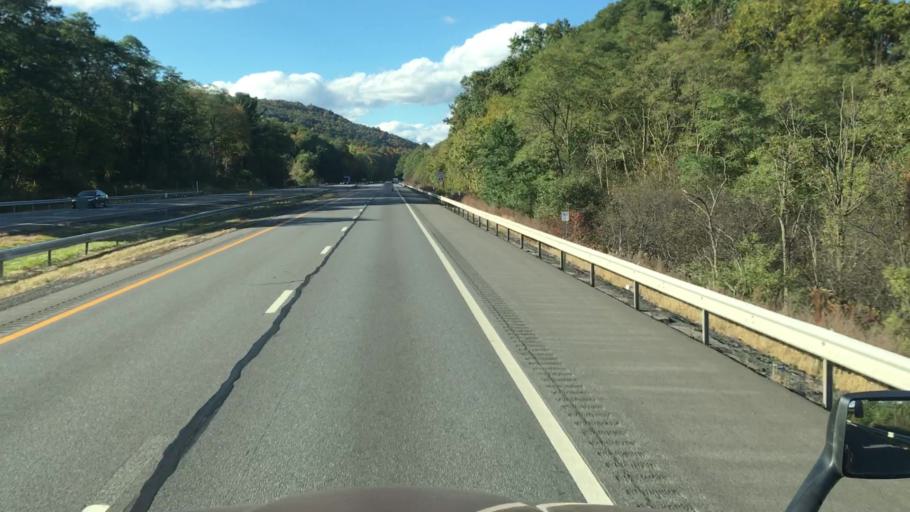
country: US
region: New York
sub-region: Schenectady County
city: Scotia
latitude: 42.8480
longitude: -74.0235
